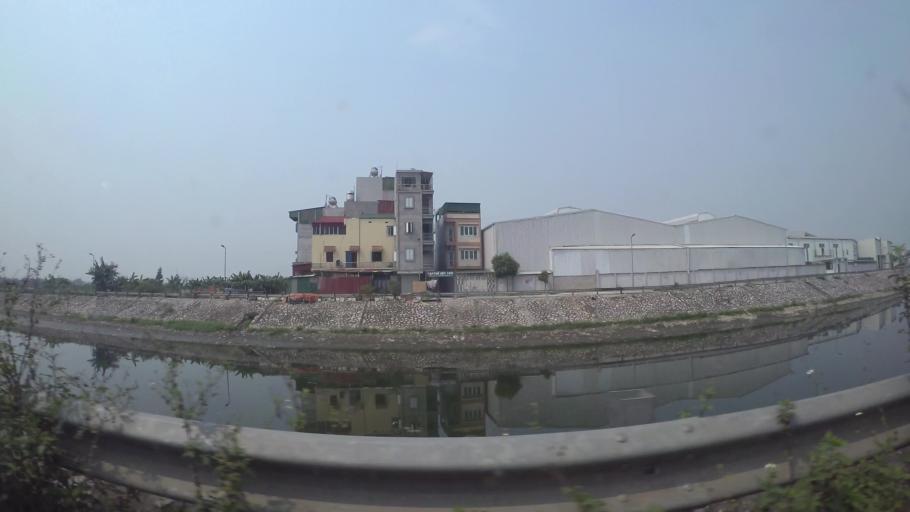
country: VN
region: Ha Noi
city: Van Dien
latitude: 20.9593
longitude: 105.8185
